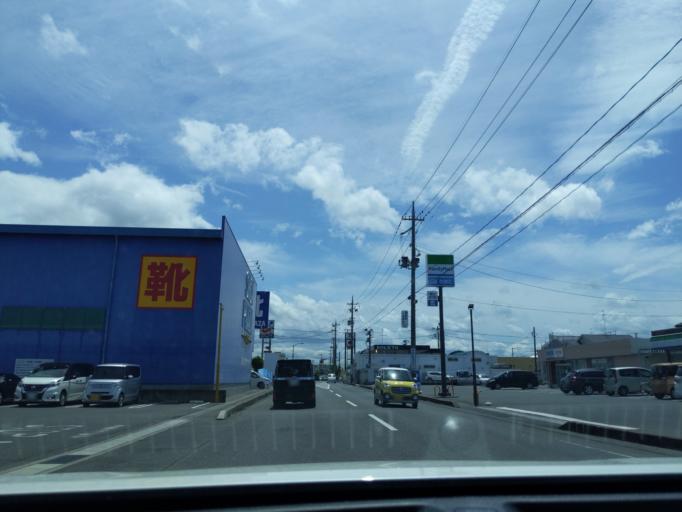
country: JP
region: Fukushima
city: Koriyama
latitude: 37.3878
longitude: 140.3325
